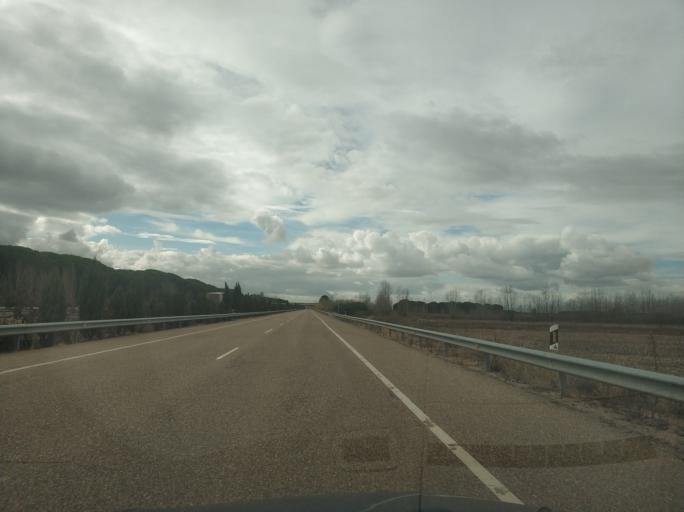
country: ES
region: Castille and Leon
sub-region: Provincia de Valladolid
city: Torrecilla de la Abadesa
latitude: 41.4710
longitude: -5.0609
